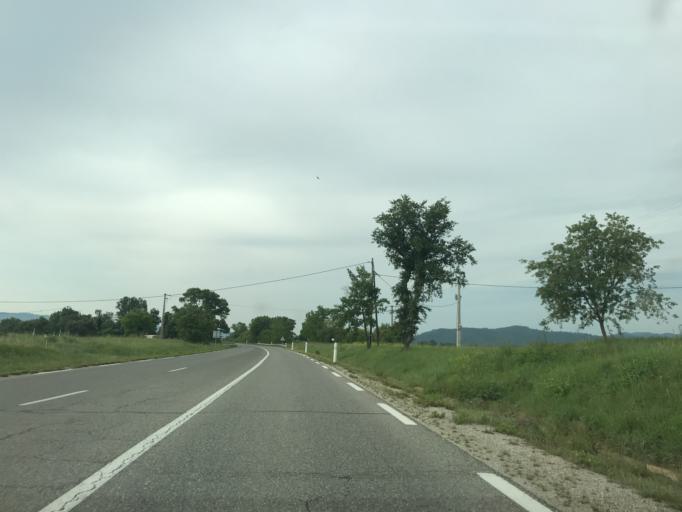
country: FR
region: Provence-Alpes-Cote d'Azur
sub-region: Departement des Alpes-de-Haute-Provence
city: Oraison
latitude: 43.9444
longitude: 5.8887
